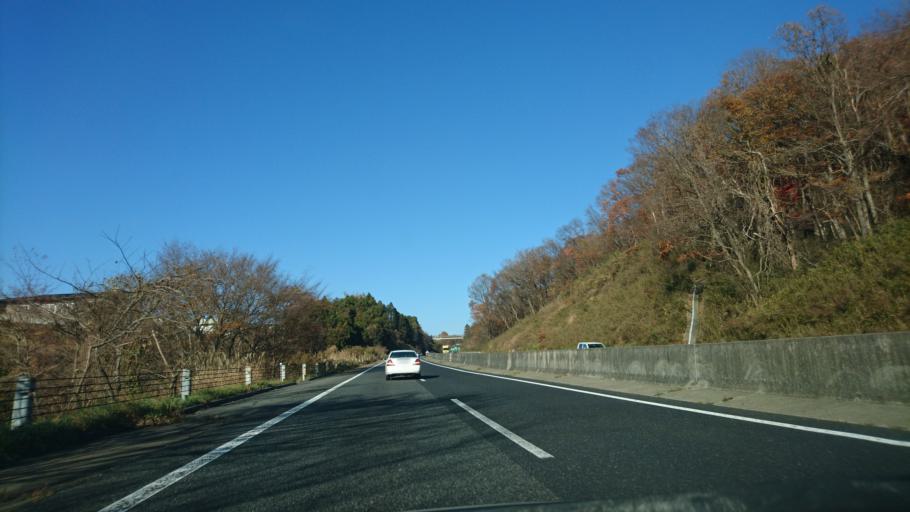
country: JP
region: Miyagi
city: Tomiya
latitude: 38.3575
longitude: 140.8815
